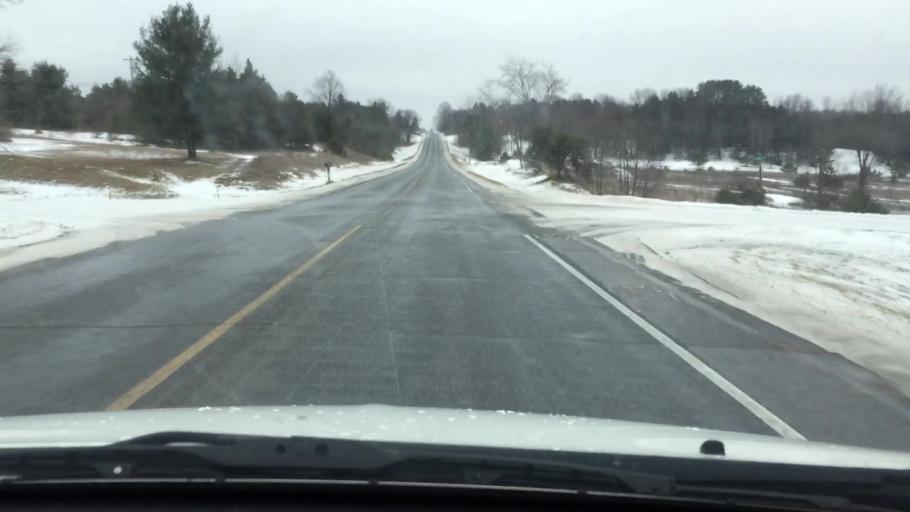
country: US
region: Michigan
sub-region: Wexford County
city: Cadillac
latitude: 44.0882
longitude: -85.4441
